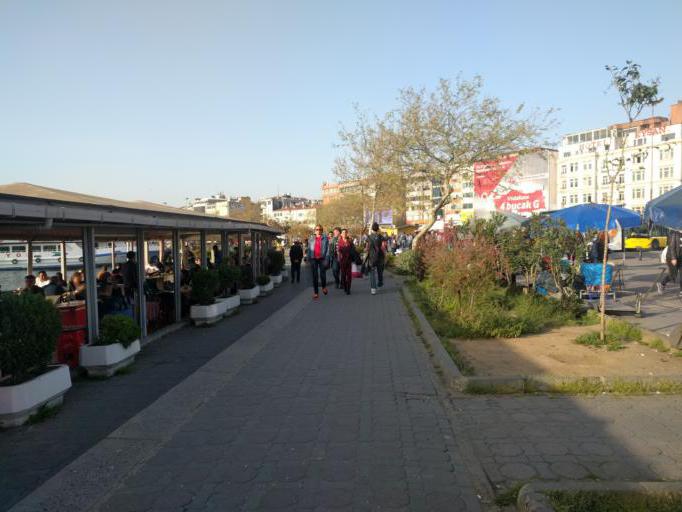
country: TR
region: Istanbul
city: UEskuedar
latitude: 40.9929
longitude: 29.0238
